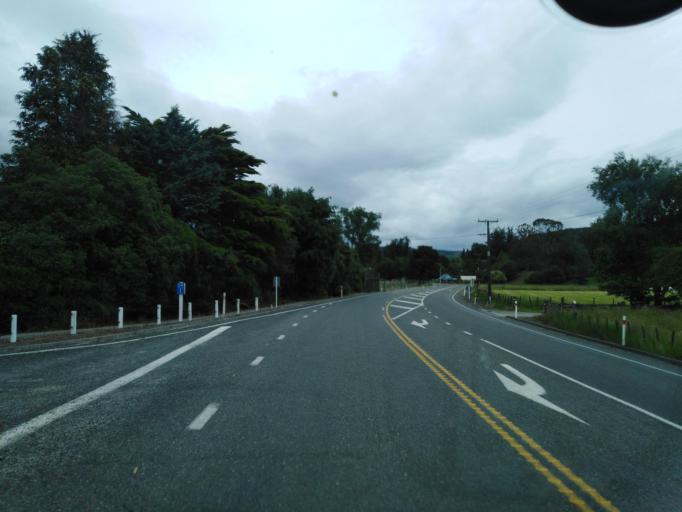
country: NZ
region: Tasman
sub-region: Tasman District
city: Wakefield
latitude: -41.4546
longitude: 172.9565
